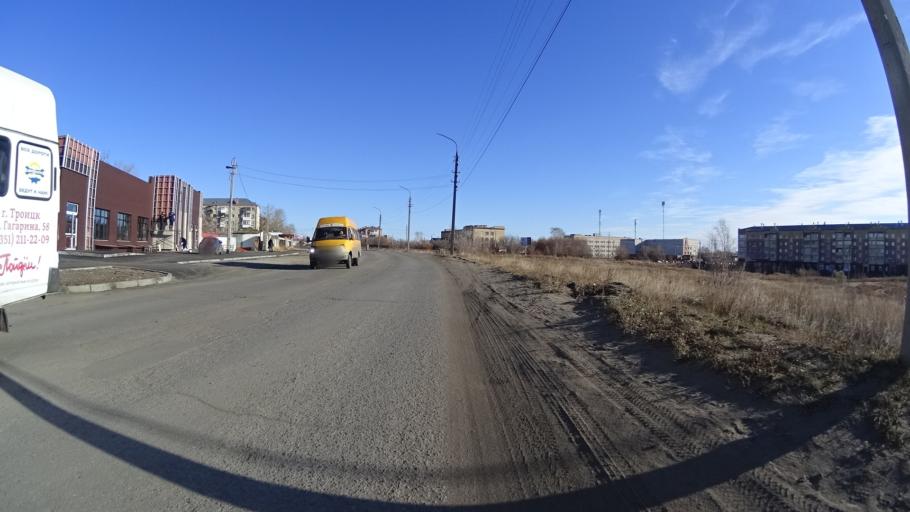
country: RU
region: Chelyabinsk
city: Troitsk
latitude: 54.0768
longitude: 61.5288
